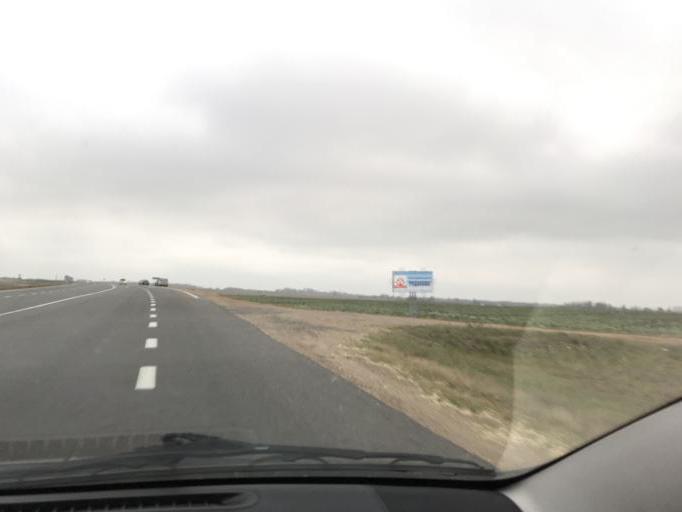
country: BY
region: Vitebsk
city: Vitebsk
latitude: 55.1601
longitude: 30.0657
